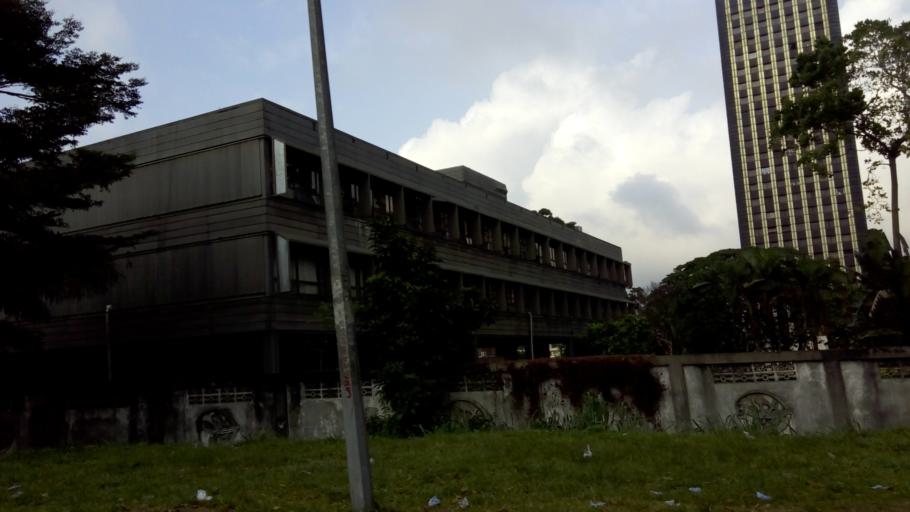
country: CI
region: Lagunes
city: Abidjan
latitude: 5.3350
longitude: -4.0249
